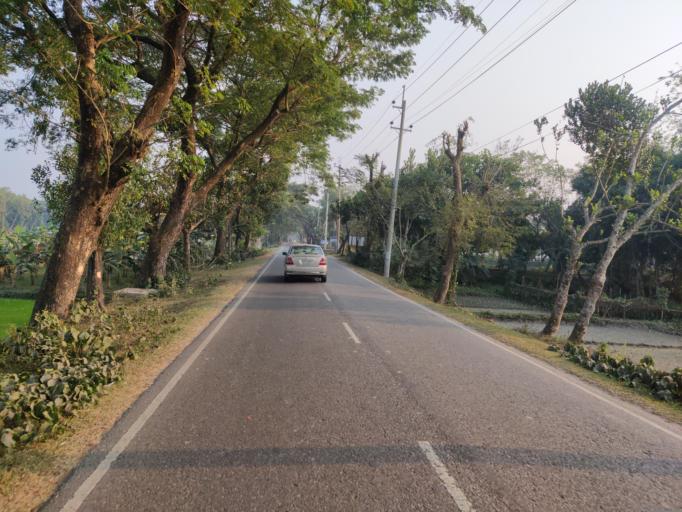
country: BD
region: Dhaka
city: Narsingdi
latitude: 24.0890
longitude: 90.7269
